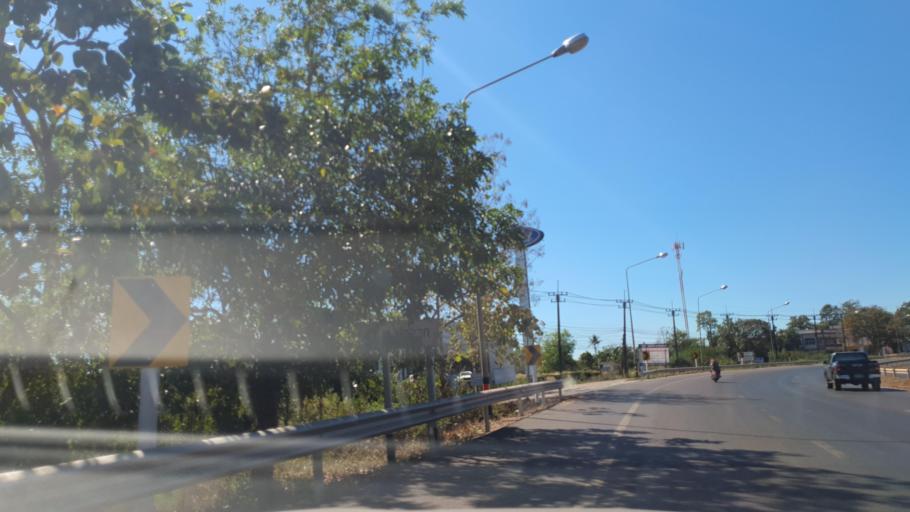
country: TH
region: Nakhon Phanom
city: Nakhon Phanom
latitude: 17.3827
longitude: 104.7571
